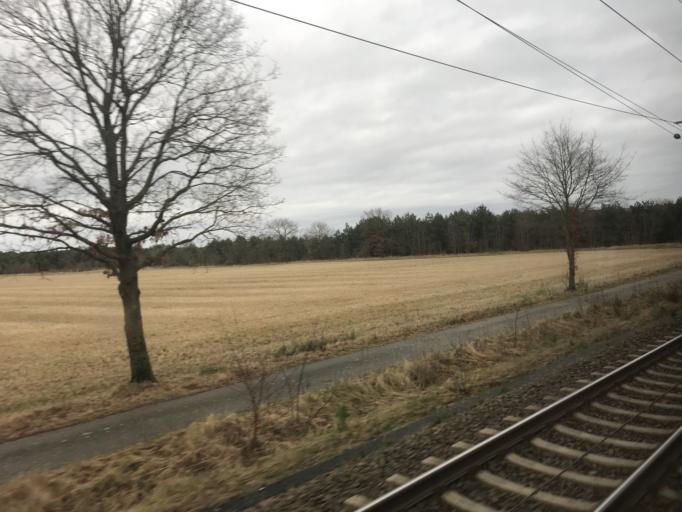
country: DE
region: Lower Saxony
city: Leiferde
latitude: 52.4566
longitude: 10.4220
